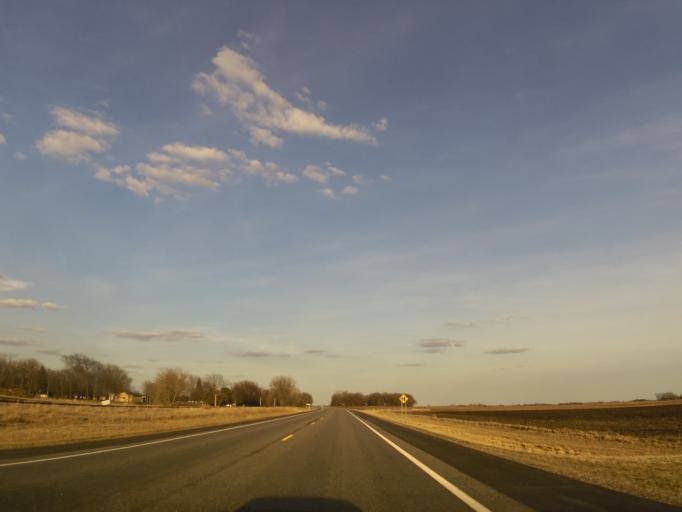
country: US
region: Minnesota
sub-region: McLeod County
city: Glencoe
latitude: 44.7393
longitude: -94.2670
